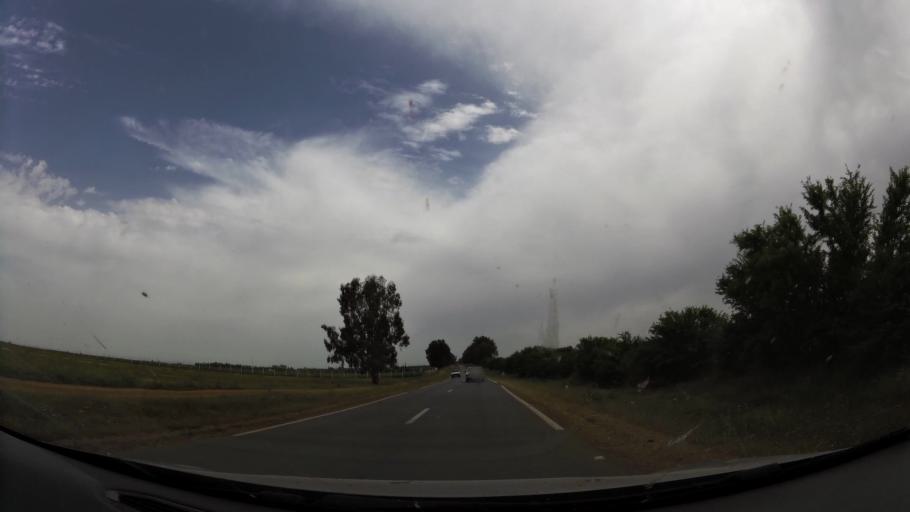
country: MA
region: Rabat-Sale-Zemmour-Zaer
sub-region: Khemisset
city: Tiflet
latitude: 33.8256
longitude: -6.2722
